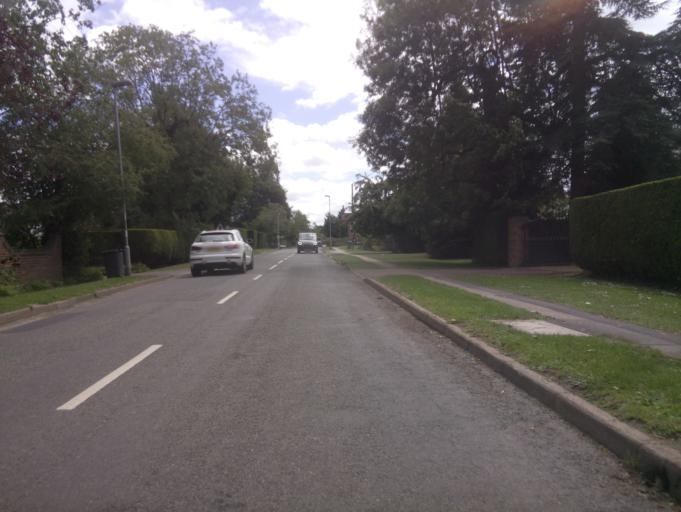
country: GB
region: England
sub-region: Nottinghamshire
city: Cotgrave
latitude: 52.8728
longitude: -1.0729
